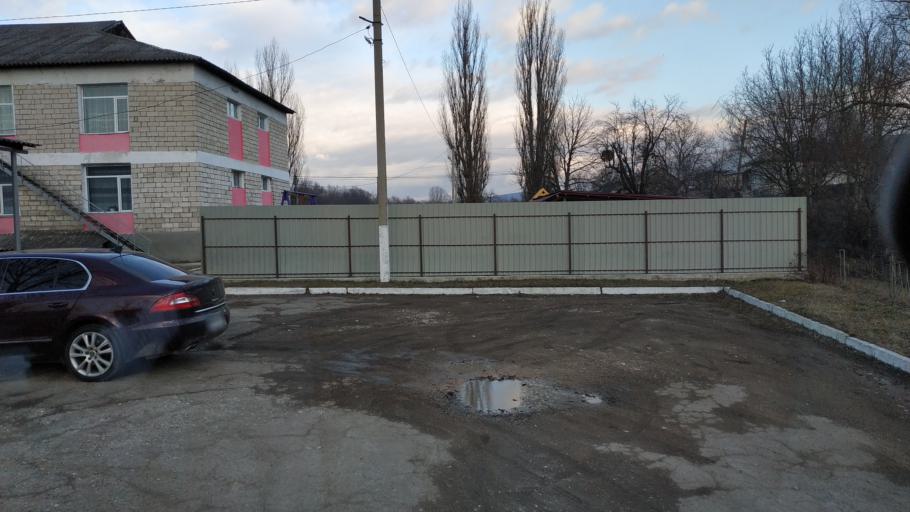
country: MD
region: Calarasi
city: Calarasi
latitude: 47.3284
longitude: 28.2215
